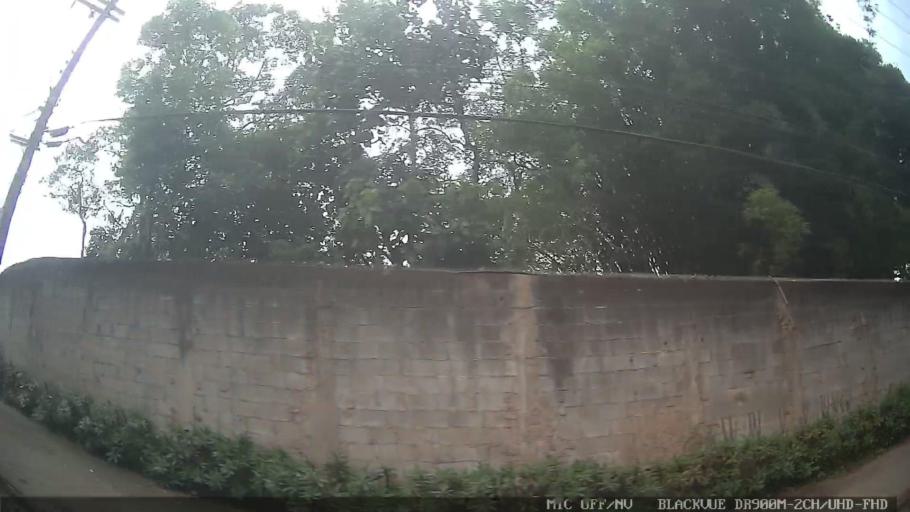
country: BR
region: Sao Paulo
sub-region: Ribeirao Pires
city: Ribeirao Pires
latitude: -23.6843
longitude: -46.3435
